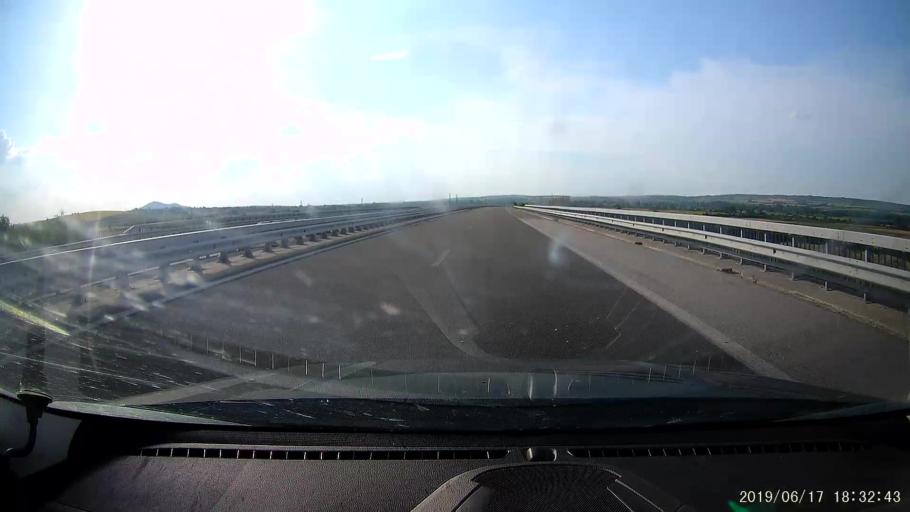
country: BG
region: Khaskovo
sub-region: Obshtina Dimitrovgrad
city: Dimitrovgrad
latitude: 42.0649
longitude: 25.4723
